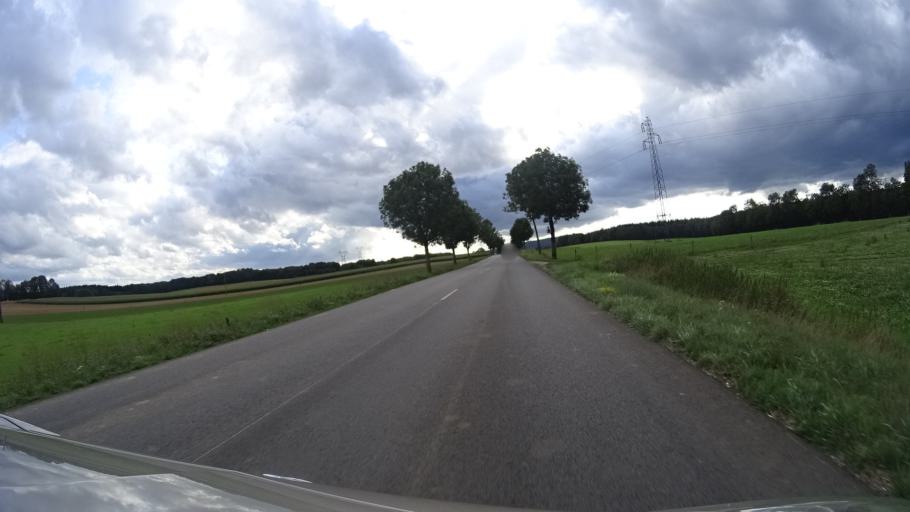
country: FR
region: Franche-Comte
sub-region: Departement du Doubs
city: Nancray
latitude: 47.2437
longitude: 6.1643
